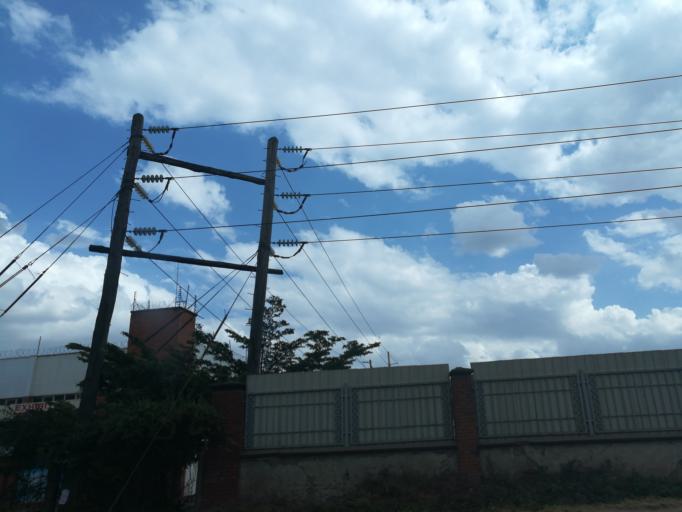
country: KE
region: Nairobi Area
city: Pumwani
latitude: -1.3306
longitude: 36.8558
